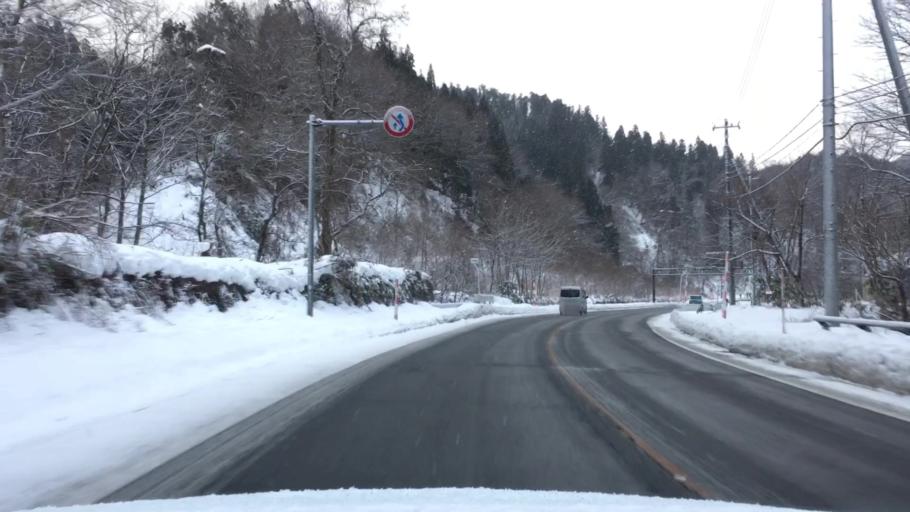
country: JP
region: Akita
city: Odate
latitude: 40.4298
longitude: 140.6371
